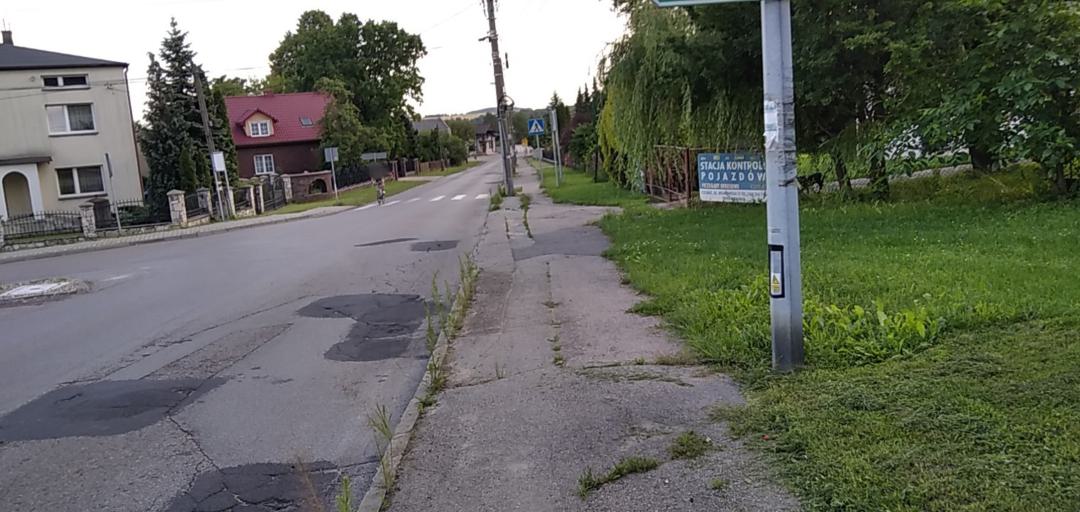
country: PL
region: Silesian Voivodeship
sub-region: Powiat bedzinski
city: Sarnow
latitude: 50.4072
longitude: 19.1390
